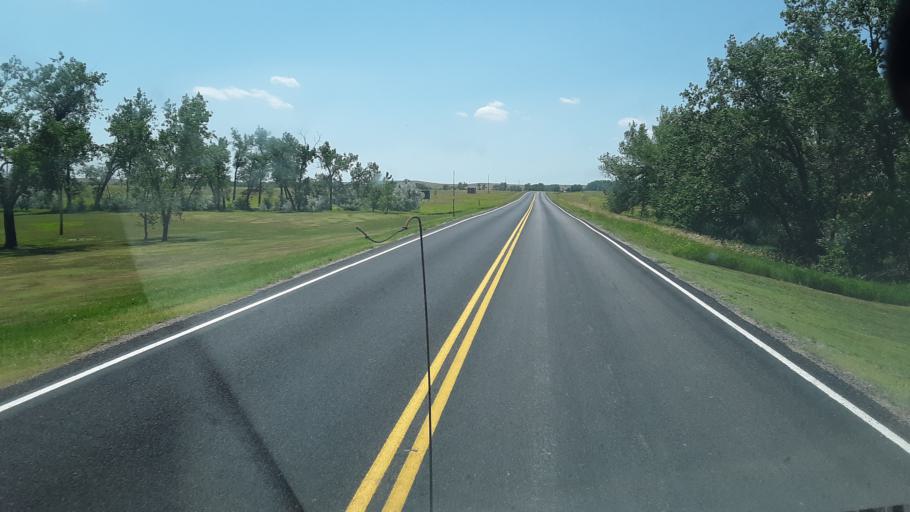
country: US
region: South Dakota
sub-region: Haakon County
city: Philip
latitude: 43.8335
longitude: -101.8997
